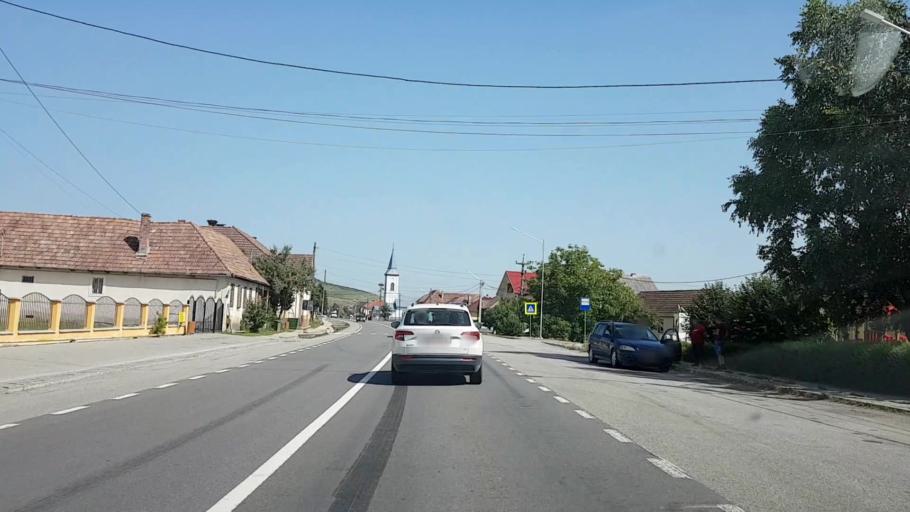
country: RO
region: Bistrita-Nasaud
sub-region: Comuna Sieu-Magherus
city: Sieu-Magherus
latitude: 47.0908
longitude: 24.3736
